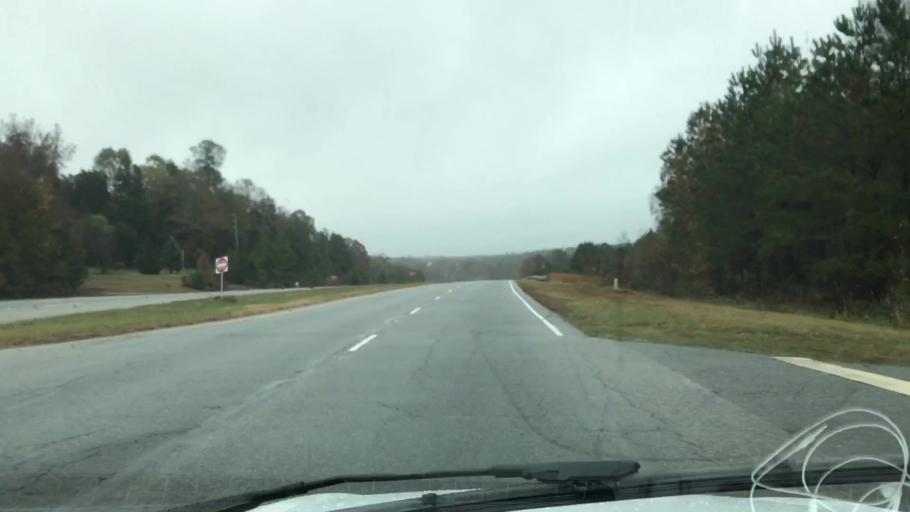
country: US
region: South Carolina
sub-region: Laurens County
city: Clinton
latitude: 34.4010
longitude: -81.9363
